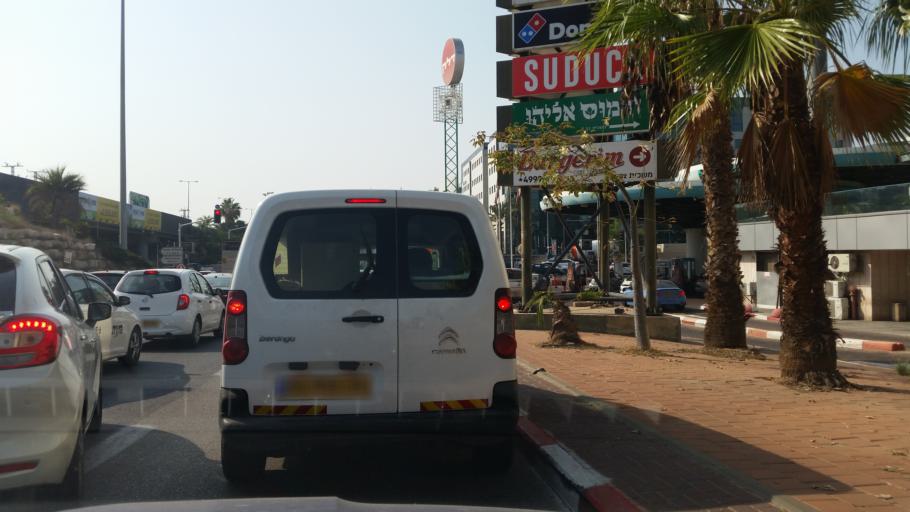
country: IL
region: Tel Aviv
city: Herzliyya
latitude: 32.1614
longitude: 34.8112
